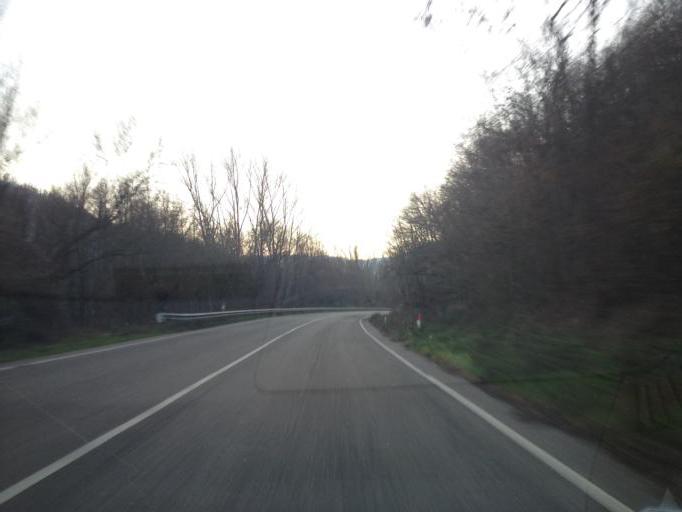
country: IT
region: The Marches
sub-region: Provincia di Ascoli Piceno
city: Arquata del Tronto
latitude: 42.7535
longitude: 13.2769
